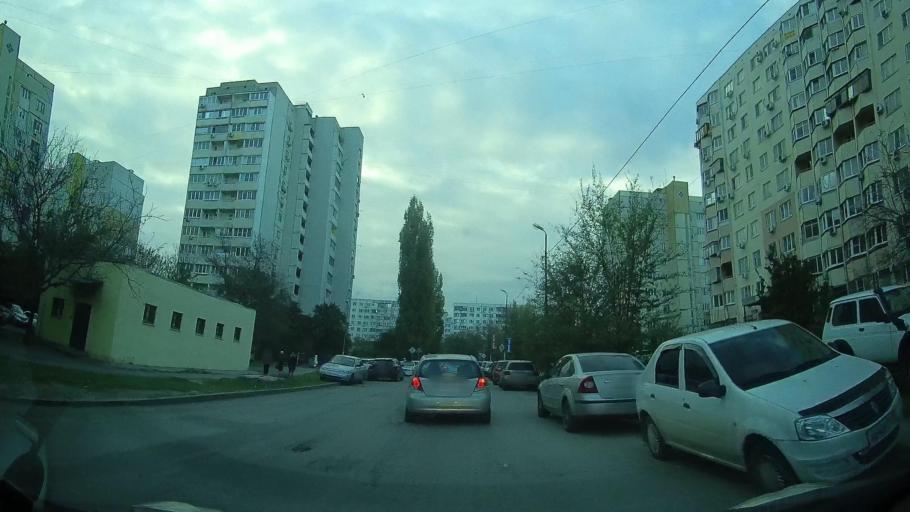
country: RU
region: Rostov
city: Severnyy
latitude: 47.2590
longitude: 39.6441
